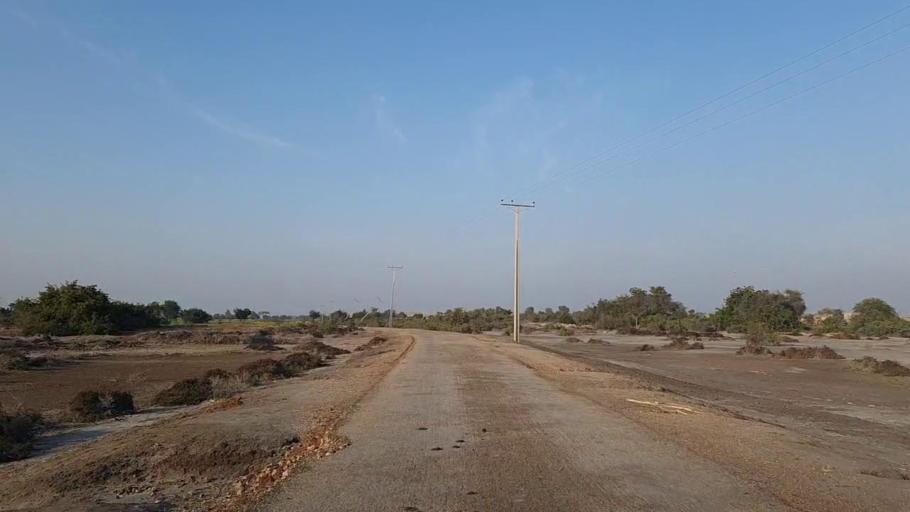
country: PK
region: Sindh
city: Jam Sahib
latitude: 26.3777
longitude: 68.5387
